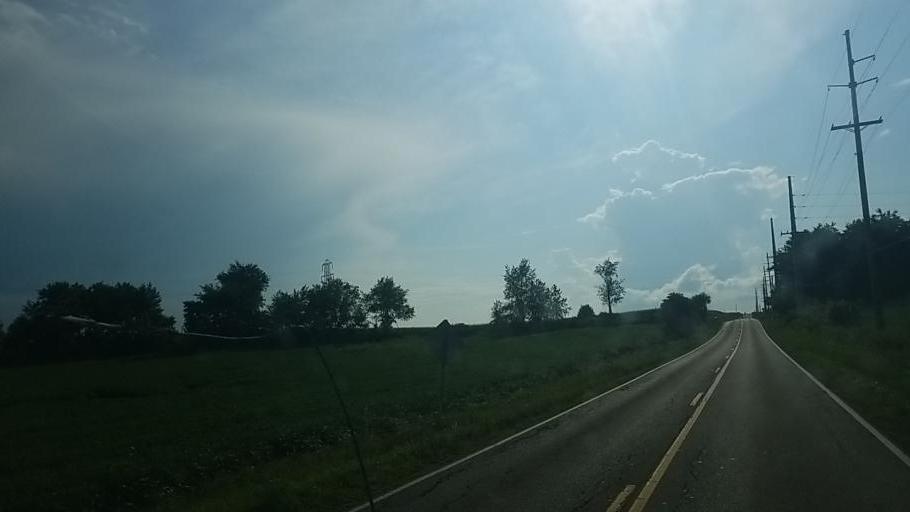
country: US
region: Ohio
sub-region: Wayne County
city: Wooster
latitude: 40.8579
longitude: -81.9369
